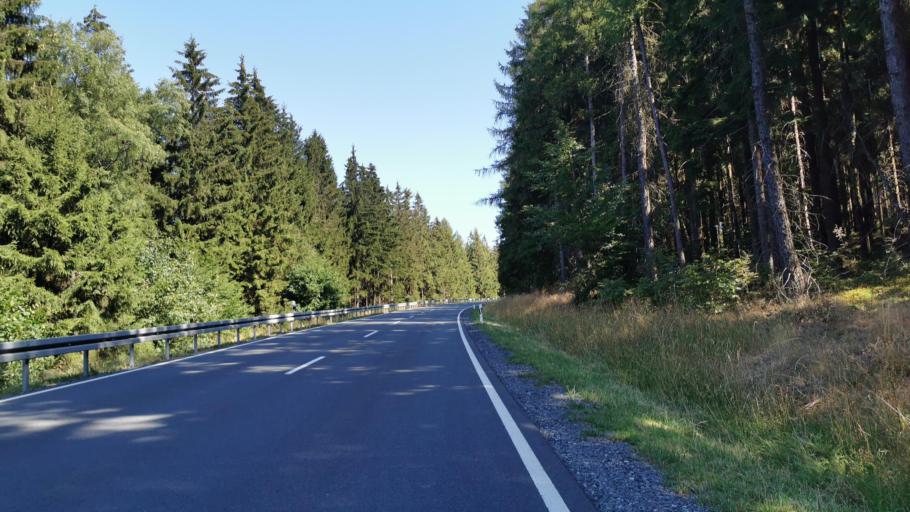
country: DE
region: Bavaria
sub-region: Upper Franconia
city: Tettau
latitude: 50.4767
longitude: 11.2937
